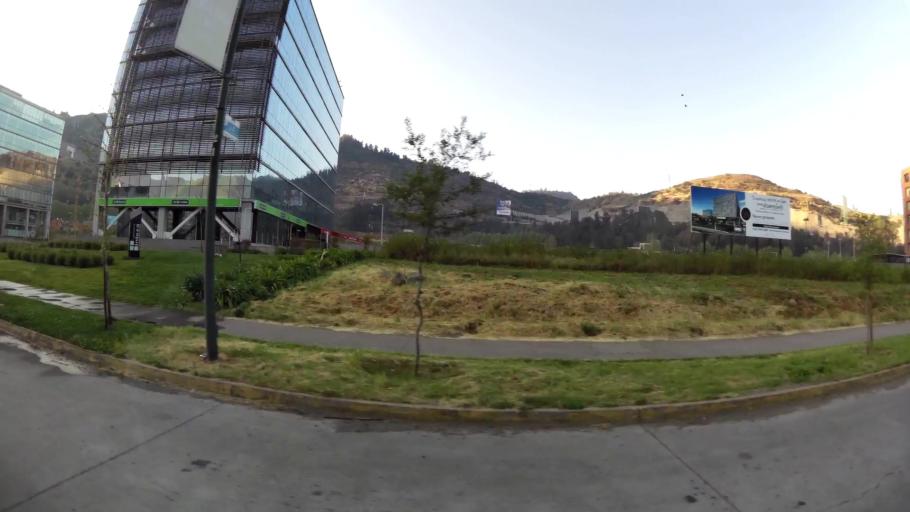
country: CL
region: Santiago Metropolitan
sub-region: Provincia de Santiago
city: Santiago
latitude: -33.3938
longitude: -70.6163
